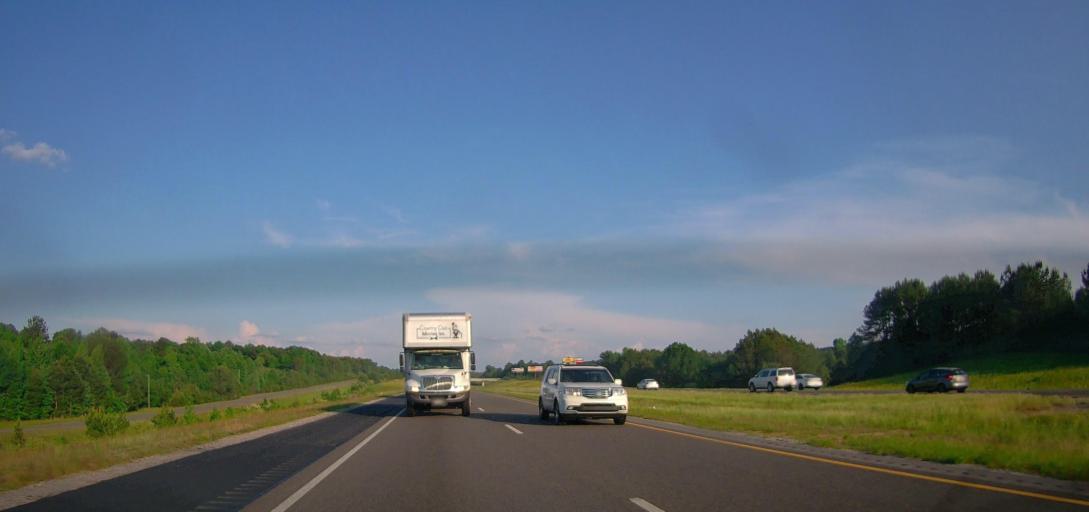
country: US
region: Alabama
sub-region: Walker County
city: Carbon Hill
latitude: 33.9310
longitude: -87.5322
